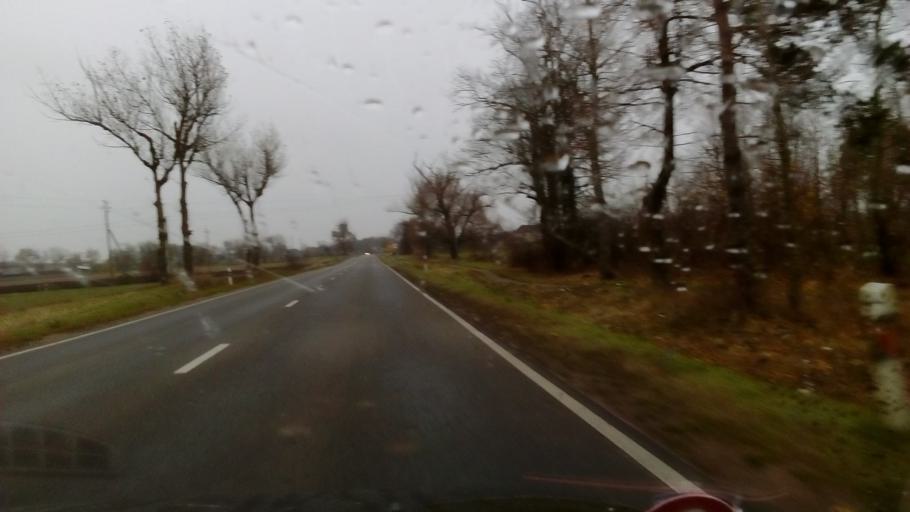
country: LT
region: Marijampoles apskritis
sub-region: Marijampole Municipality
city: Marijampole
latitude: 54.5504
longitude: 23.3988
